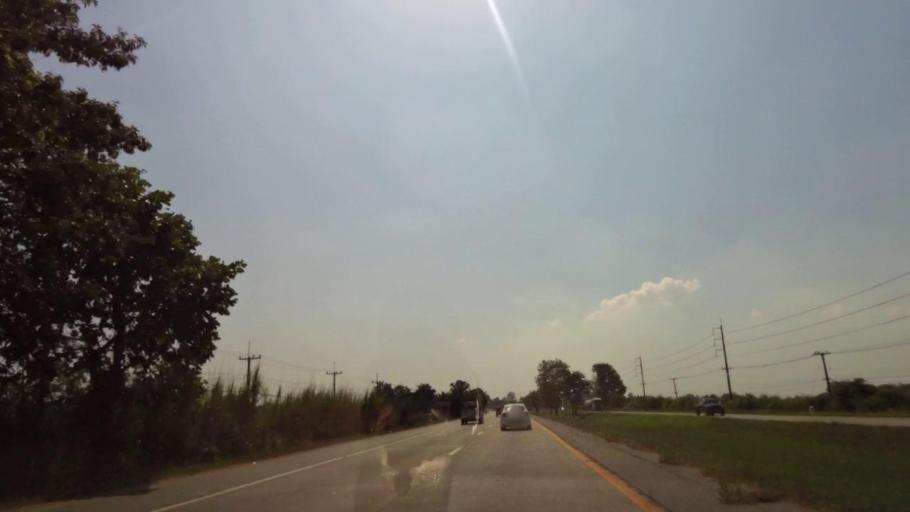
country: TH
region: Phichit
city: Wachira Barami
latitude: 16.5939
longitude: 100.1474
